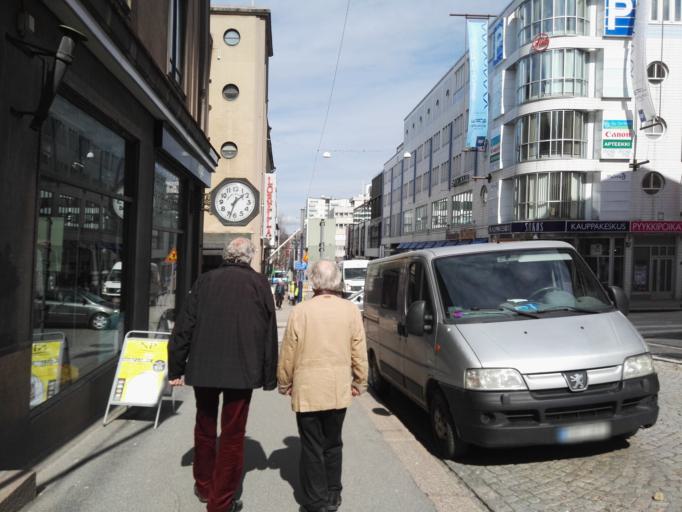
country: FI
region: Paijanne Tavastia
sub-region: Lahti
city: Lahti
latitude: 60.9815
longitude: 25.6585
